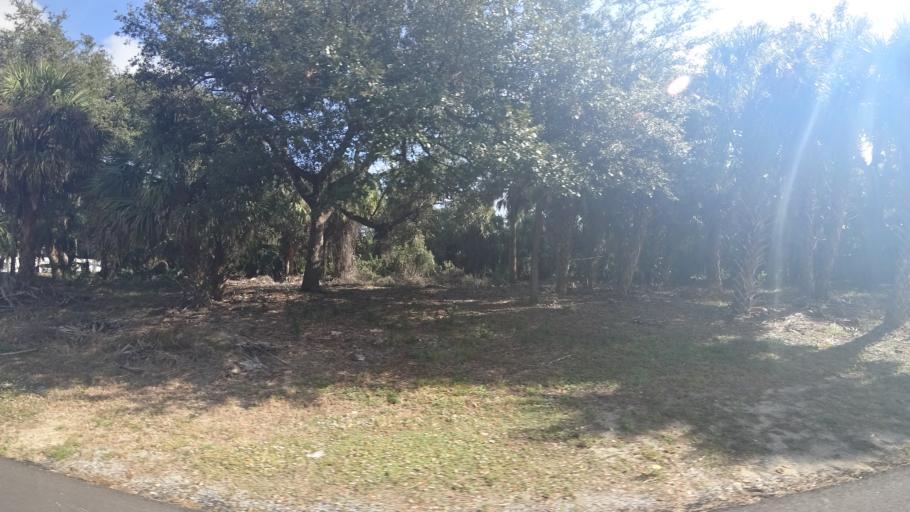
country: US
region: Florida
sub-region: Charlotte County
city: Port Charlotte
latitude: 27.0613
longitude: -82.1174
